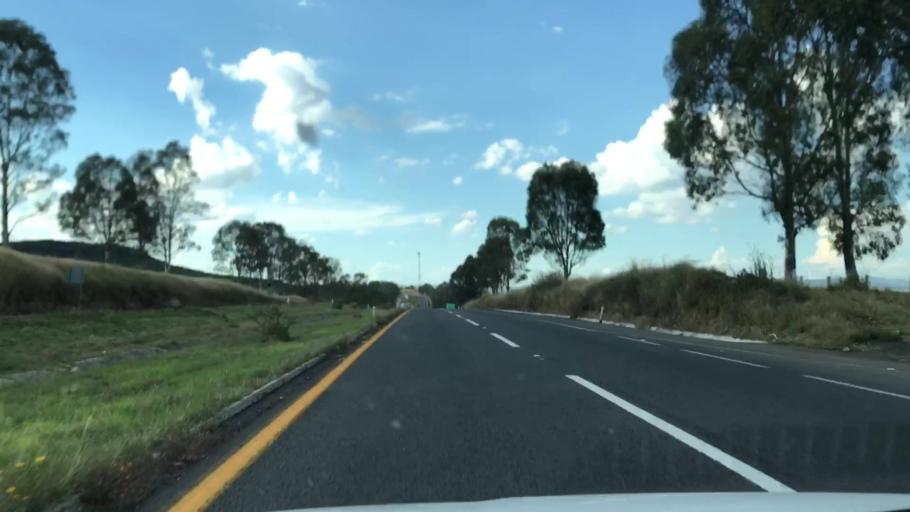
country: MX
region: Jalisco
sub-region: Lagos de Moreno
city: Cristeros [Fraccionamiento]
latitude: 21.2553
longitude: -101.9518
